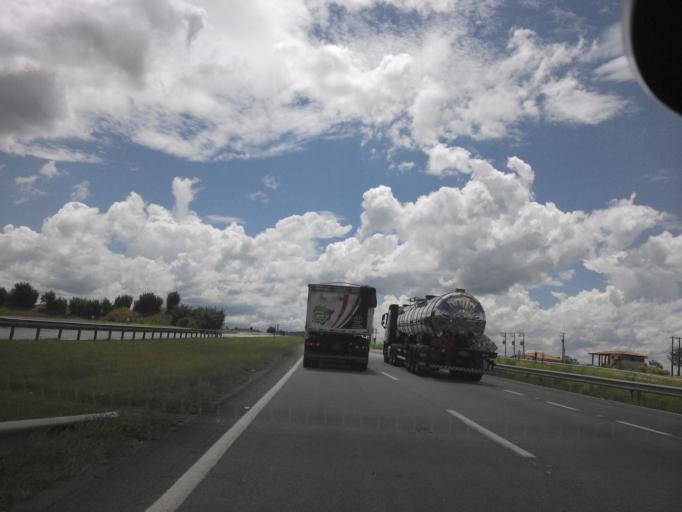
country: BR
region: Sao Paulo
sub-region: Jacarei
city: Jacarei
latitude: -23.2867
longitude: -46.0478
